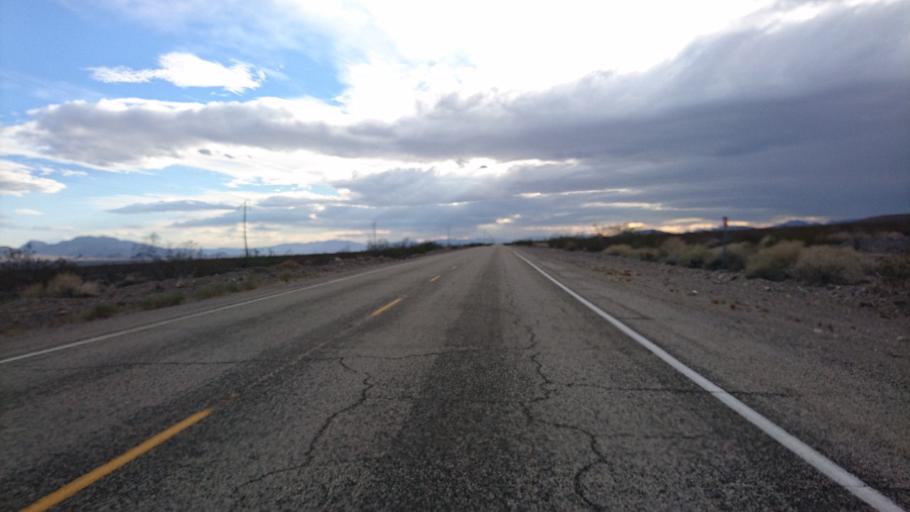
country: US
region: California
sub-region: San Bernardino County
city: Needles
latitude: 34.6635
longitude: -115.3500
